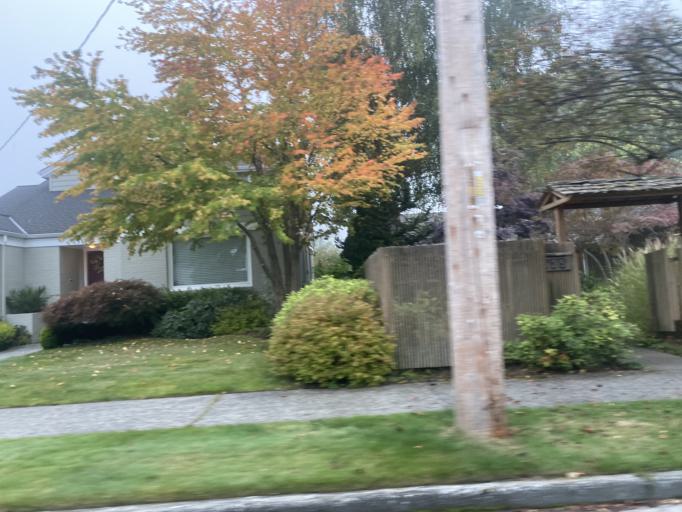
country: US
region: Washington
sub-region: King County
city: Seattle
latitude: 47.6520
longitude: -122.4129
